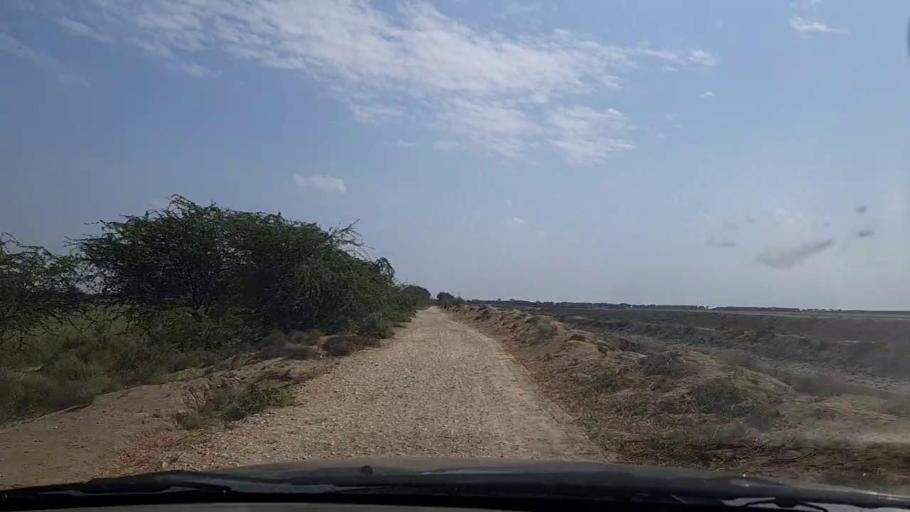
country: PK
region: Sindh
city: Mirpur Batoro
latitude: 24.5727
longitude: 68.1970
